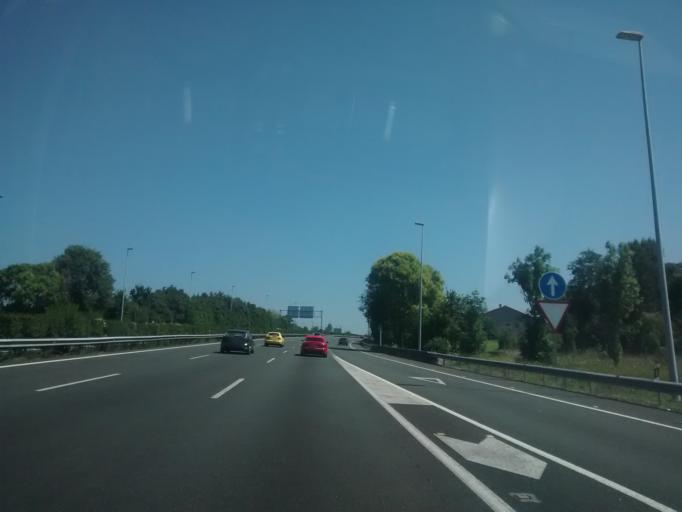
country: ES
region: Cantabria
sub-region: Provincia de Cantabria
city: Entrambasaguas
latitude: 43.3901
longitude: -3.6627
